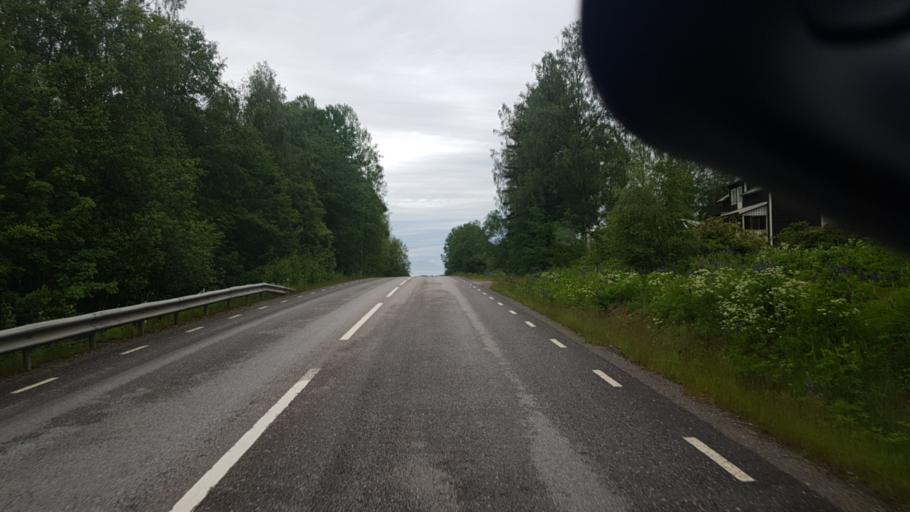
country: SE
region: Vaermland
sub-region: Eda Kommun
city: Amotfors
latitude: 59.7211
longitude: 12.1696
